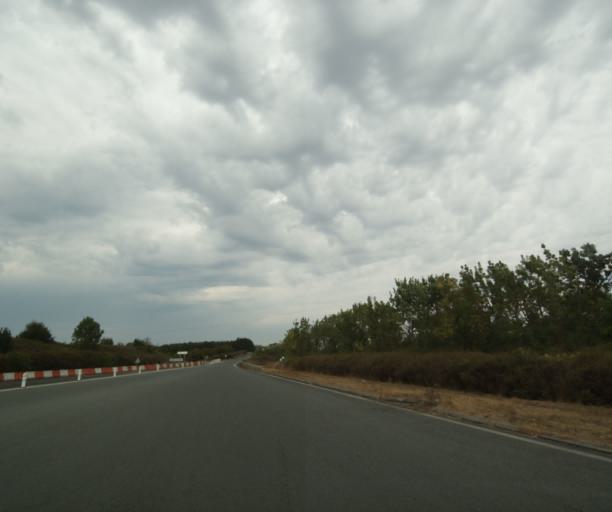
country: FR
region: Poitou-Charentes
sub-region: Departement de la Charente-Maritime
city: Tonnay-Charente
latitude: 45.9558
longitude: -0.8821
